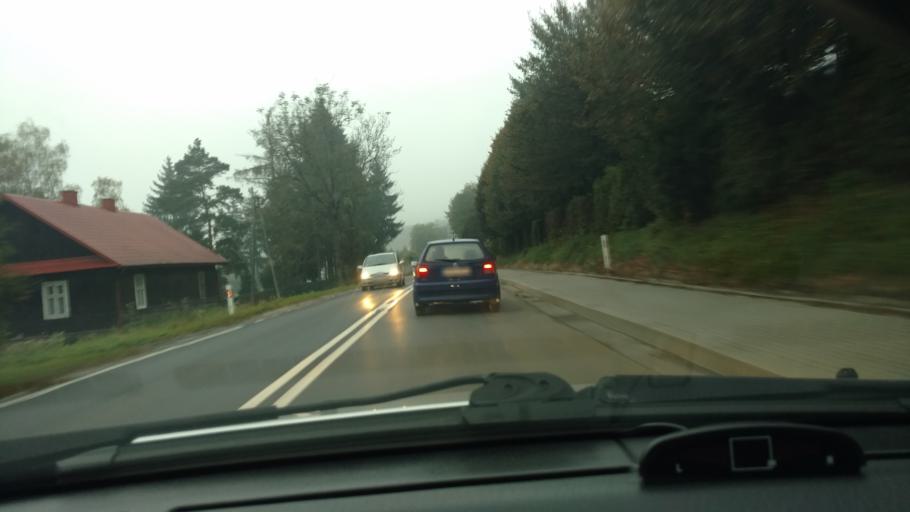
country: PL
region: Subcarpathian Voivodeship
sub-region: Powiat strzyzowski
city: Wysoka Strzyzowska
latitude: 49.8780
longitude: 21.7233
